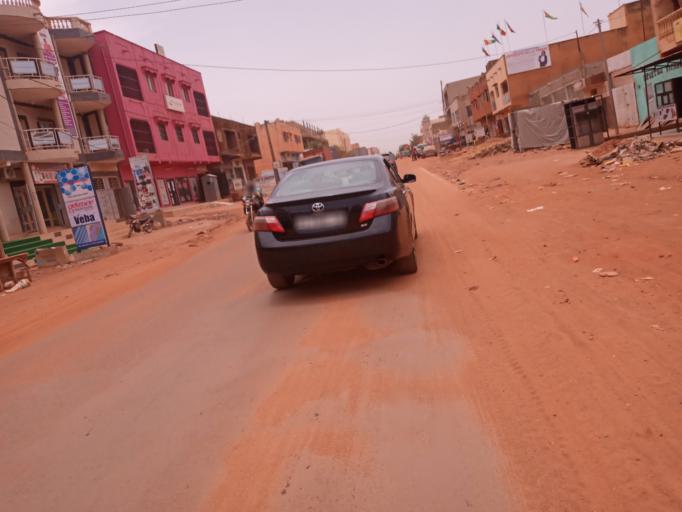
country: ML
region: Bamako
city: Bamako
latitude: 12.5803
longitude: -8.0179
